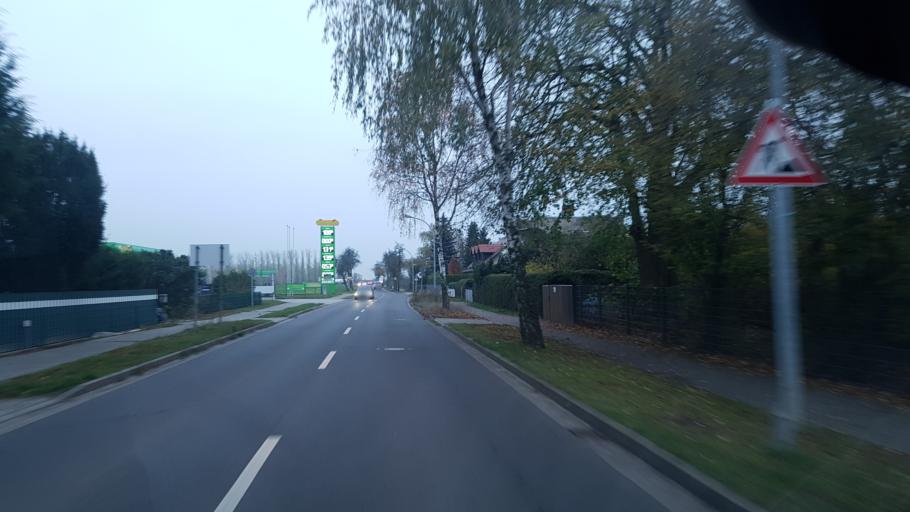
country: DE
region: Brandenburg
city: Fehrbellin
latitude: 52.8057
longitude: 12.7866
